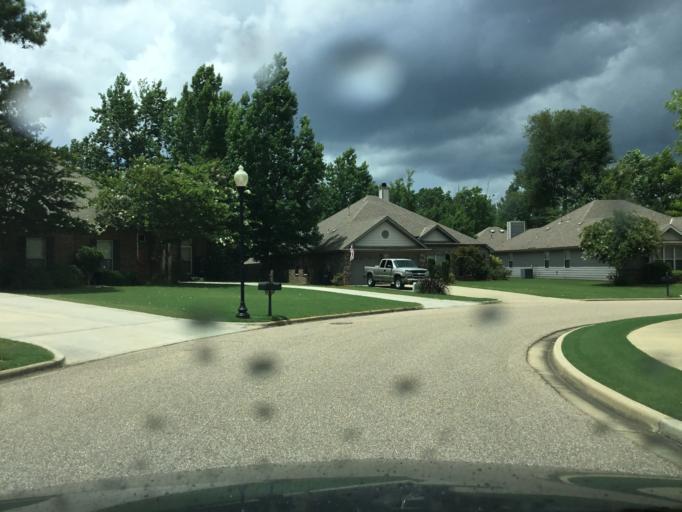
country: US
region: Alabama
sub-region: Montgomery County
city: Pike Road
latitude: 32.3424
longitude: -86.0827
